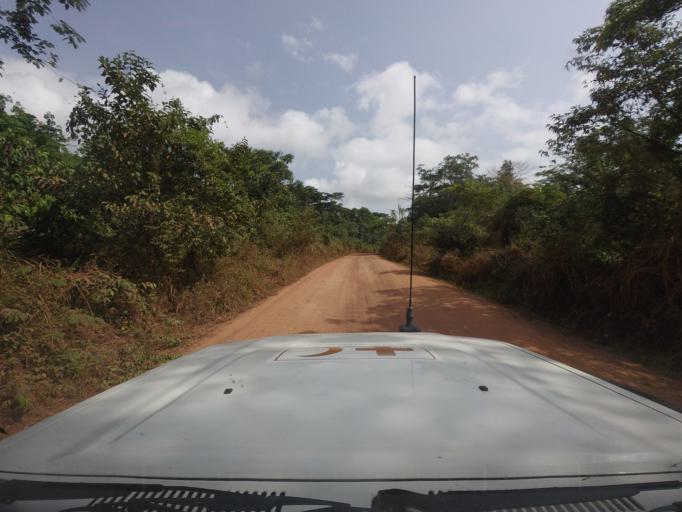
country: LR
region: Bong
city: Gbarnga
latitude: 7.2214
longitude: -9.4386
